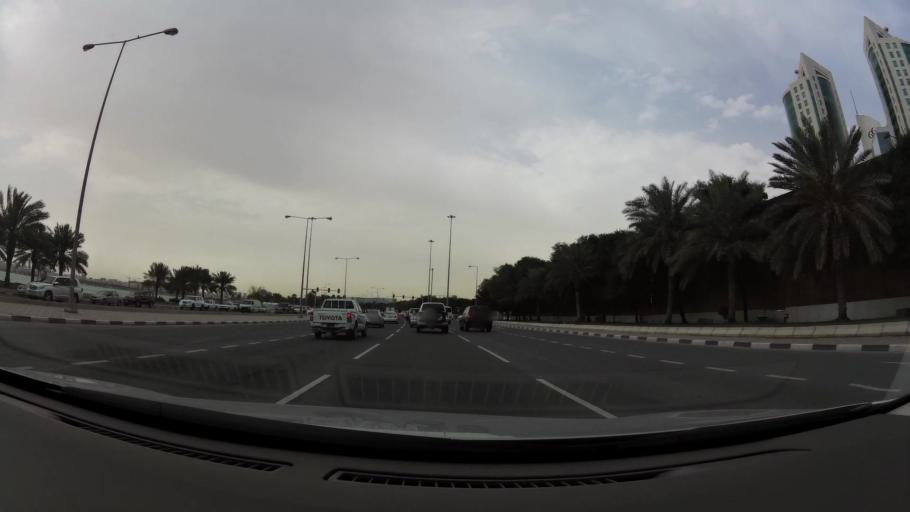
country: QA
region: Baladiyat ad Dawhah
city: Doha
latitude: 25.3126
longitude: 51.5210
